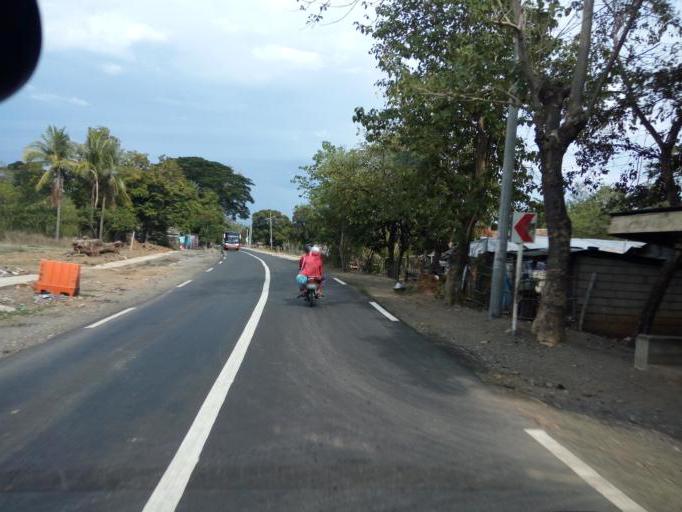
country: PH
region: Central Luzon
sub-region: Province of Nueva Ecija
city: Parista
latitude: 15.8273
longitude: 120.9480
